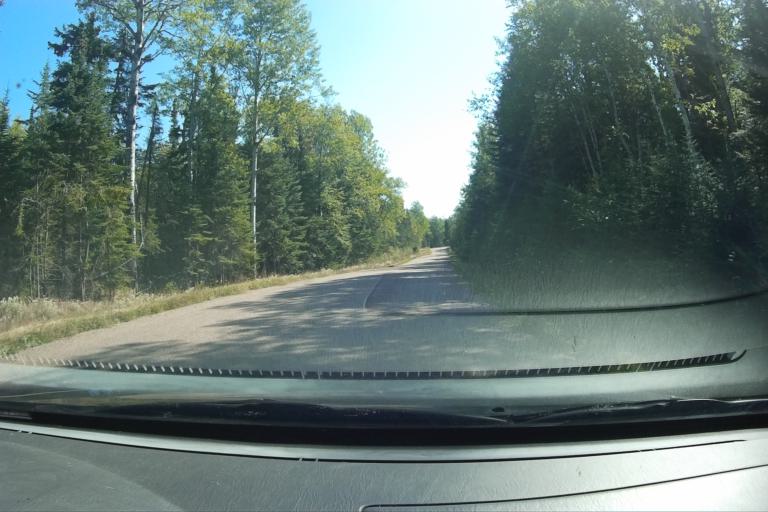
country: CA
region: Ontario
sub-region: Thunder Bay District
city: Thunder Bay
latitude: 48.3477
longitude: -88.8003
